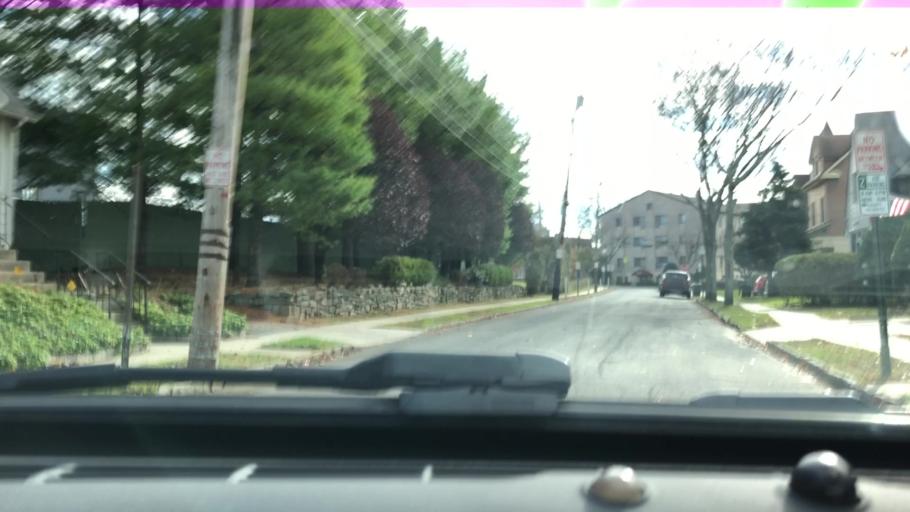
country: US
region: New York
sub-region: Westchester County
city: Tuckahoe
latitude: 40.9608
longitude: -73.8125
